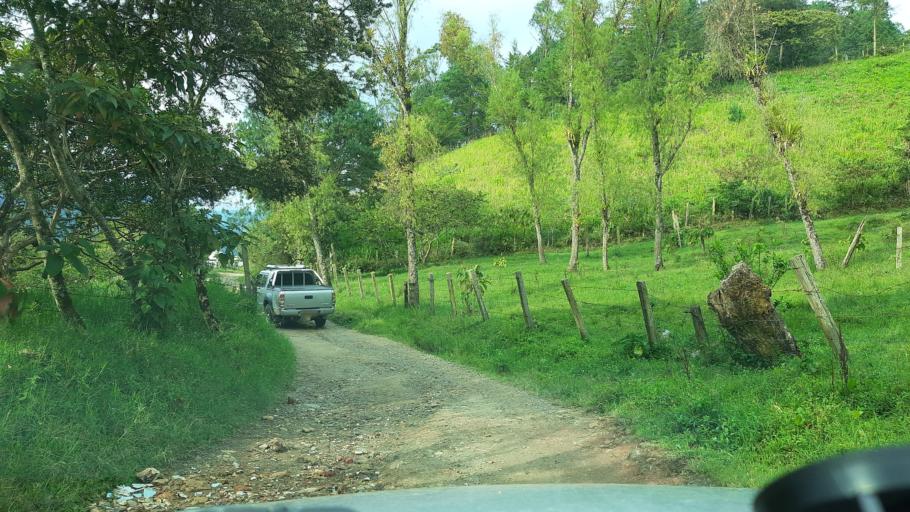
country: CO
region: Boyaca
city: Garagoa
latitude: 5.0759
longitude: -73.3611
